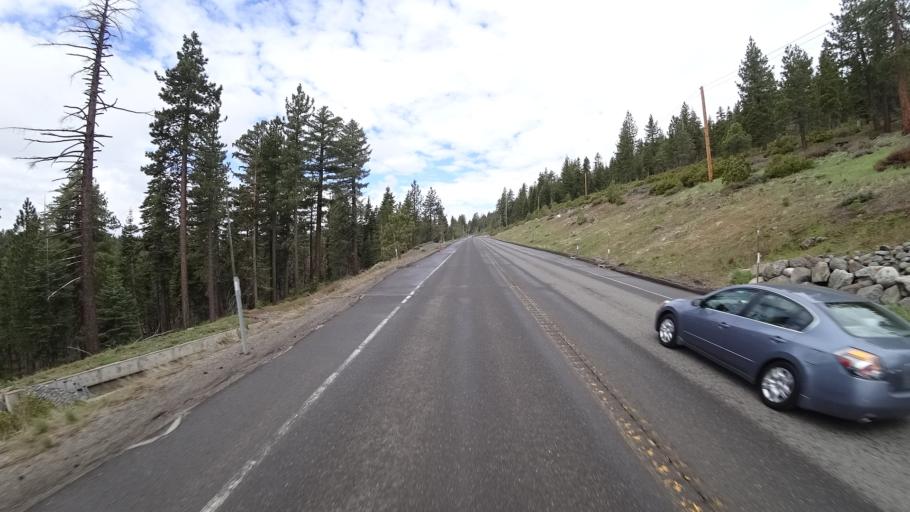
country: US
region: California
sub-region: Placer County
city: Tahoe Vista
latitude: 39.2580
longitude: -120.0568
